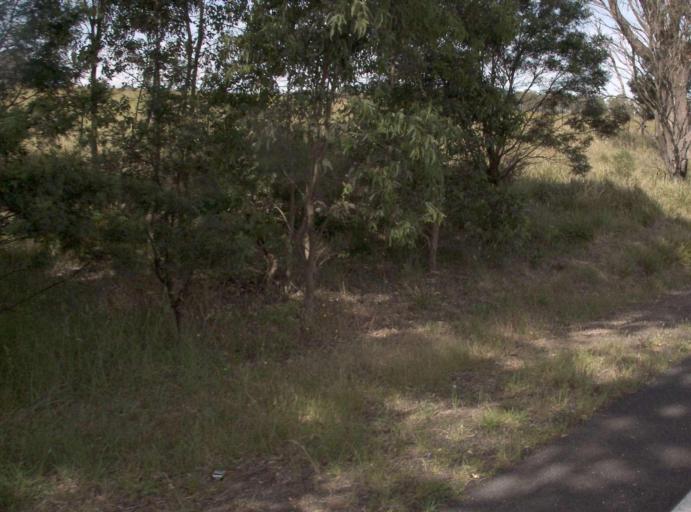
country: AU
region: Victoria
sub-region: East Gippsland
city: Lakes Entrance
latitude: -37.8191
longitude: 147.8231
